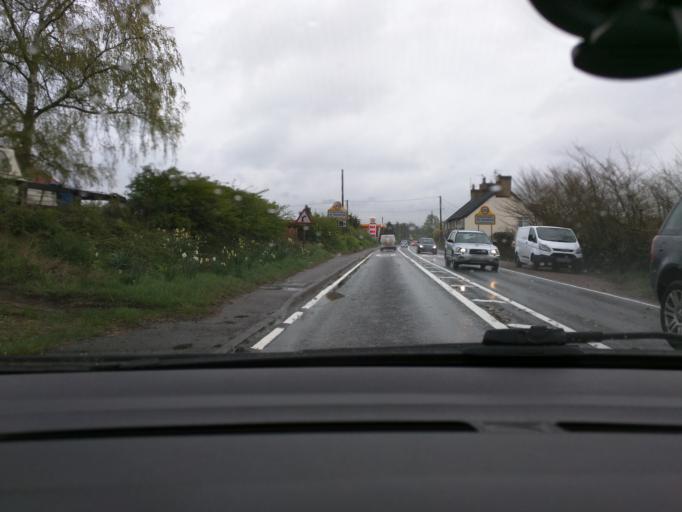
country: GB
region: England
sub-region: Suffolk
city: Saxmundham
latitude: 52.1873
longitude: 1.4468
